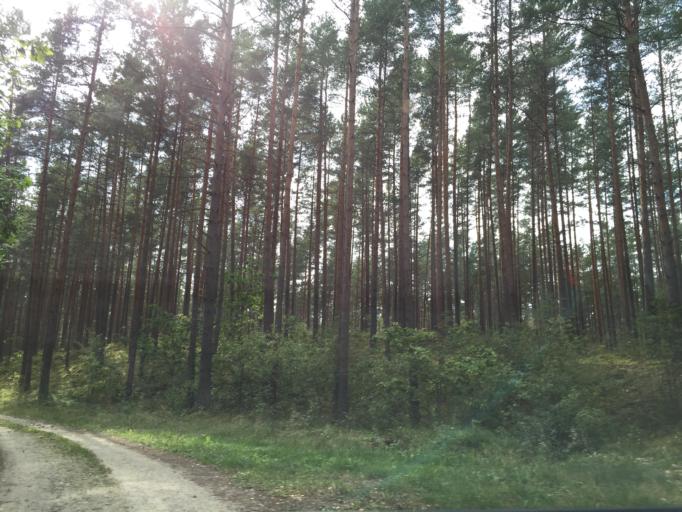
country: LV
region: Jurmala
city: Jurmala
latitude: 56.8818
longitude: 23.7474
